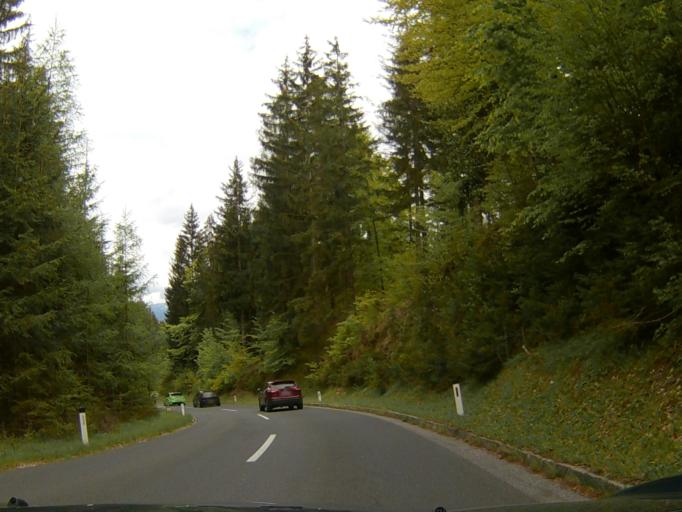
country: AT
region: Carinthia
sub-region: Villach Stadt
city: Villach
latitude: 46.5791
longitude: 13.7858
